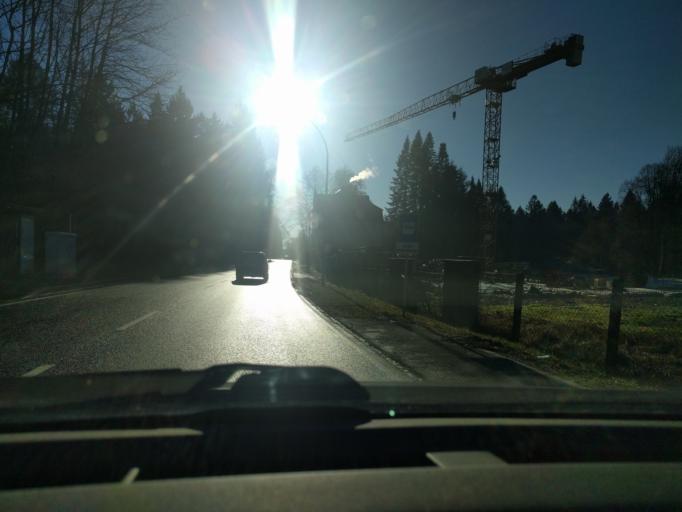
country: LU
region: Diekirch
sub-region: Canton de Clervaux
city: Weiswampach
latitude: 50.1554
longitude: 6.0523
